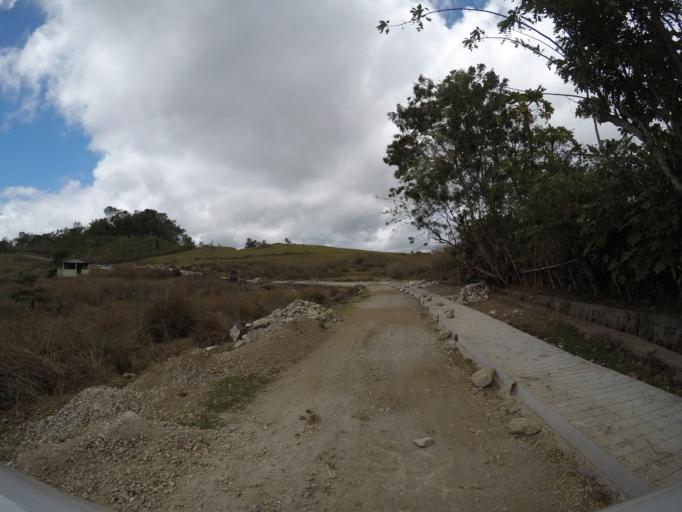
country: TL
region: Lautem
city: Lospalos
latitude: -8.5554
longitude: 126.8297
